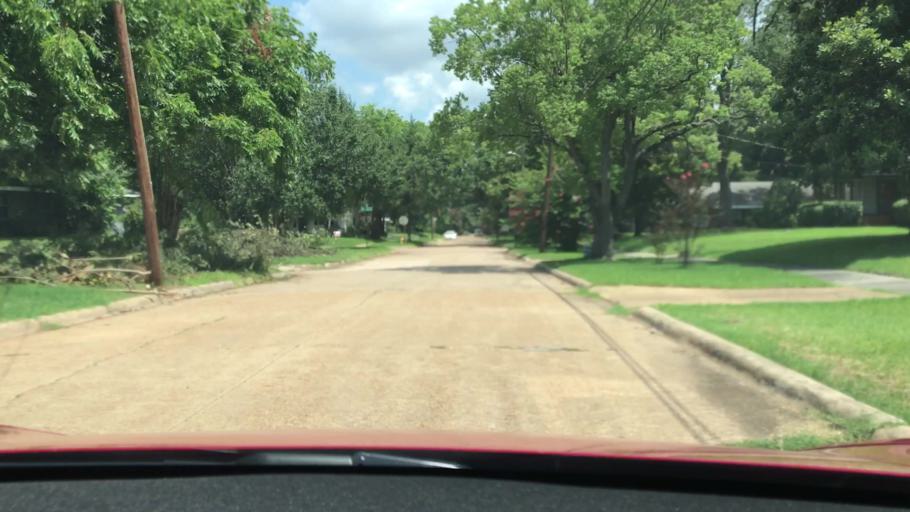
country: US
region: Louisiana
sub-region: Bossier Parish
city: Bossier City
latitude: 32.4574
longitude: -93.7259
